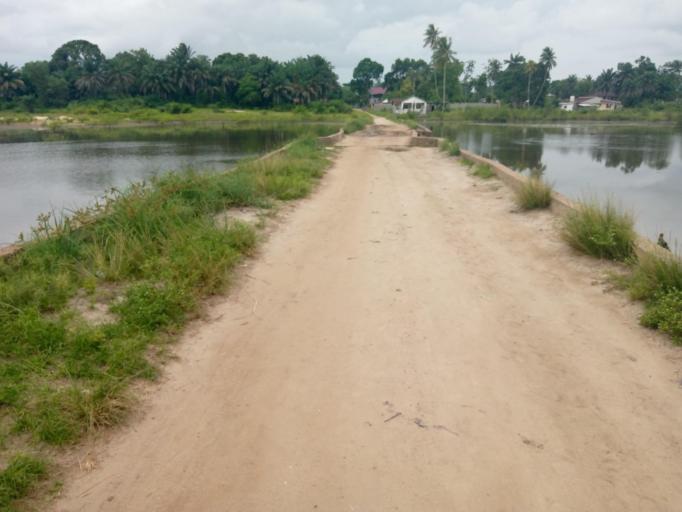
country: SL
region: Southern Province
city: Bonthe
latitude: 7.5281
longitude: -12.5029
